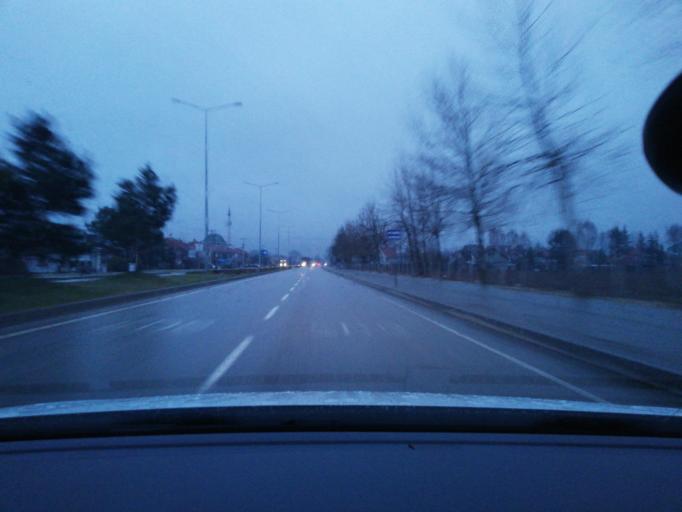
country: TR
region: Bolu
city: Bolu
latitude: 40.7091
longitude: 31.6165
